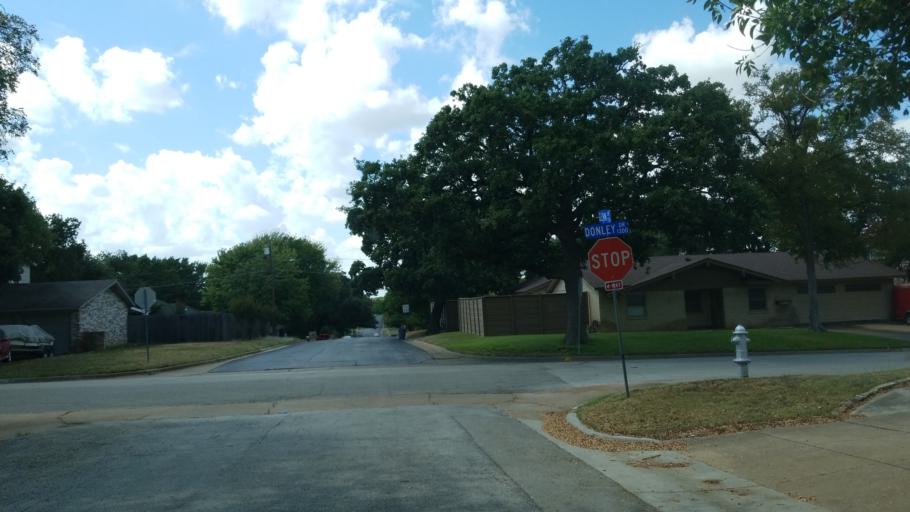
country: US
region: Texas
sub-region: Tarrant County
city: Euless
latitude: 32.8555
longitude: -97.0938
